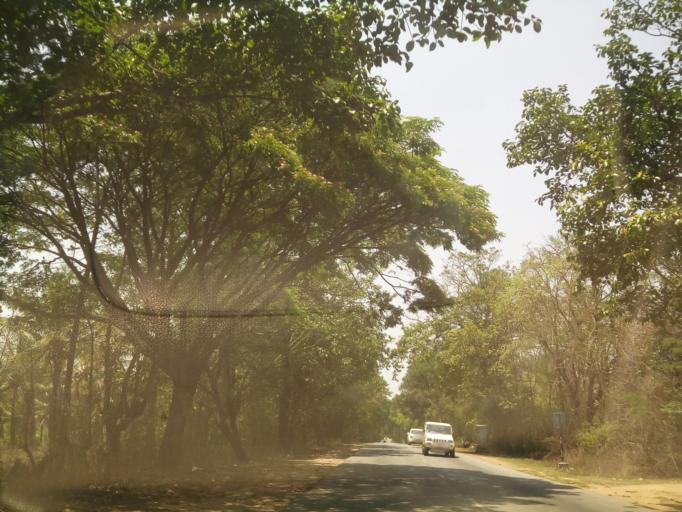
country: IN
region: Karnataka
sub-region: Hassan
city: Alur
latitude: 12.9583
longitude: 75.9827
